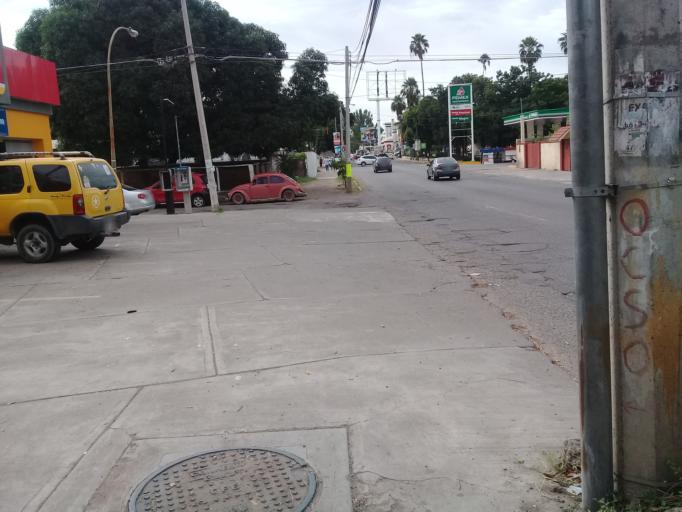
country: MX
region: Sinaloa
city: Culiacan
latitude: 24.8186
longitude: -107.3962
